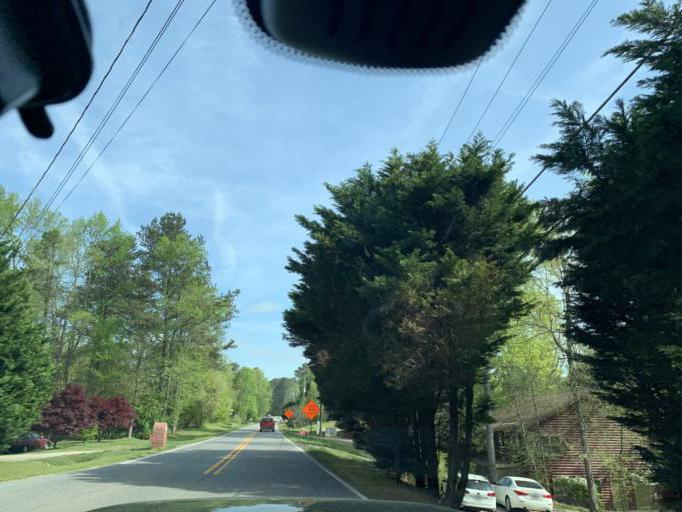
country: US
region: Georgia
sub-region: Forsyth County
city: Cumming
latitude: 34.2282
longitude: -84.0833
